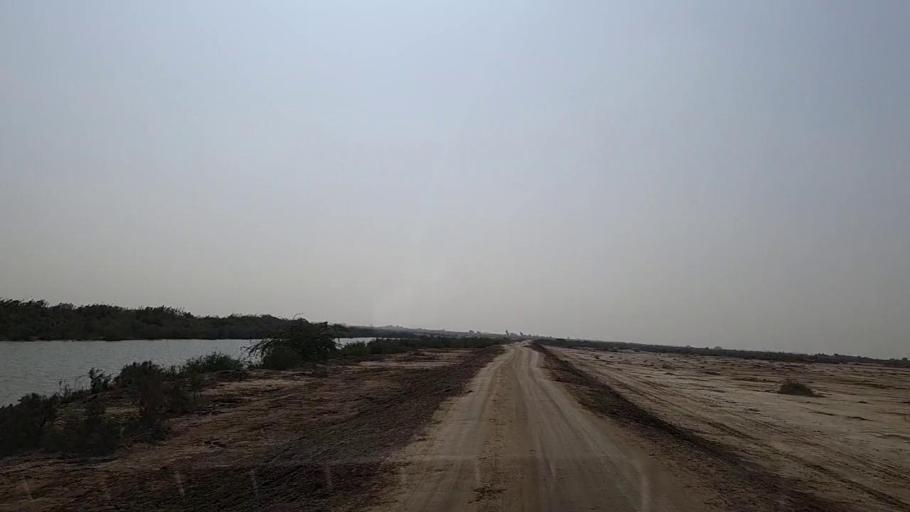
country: PK
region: Sindh
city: Gharo
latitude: 24.6788
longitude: 67.7340
